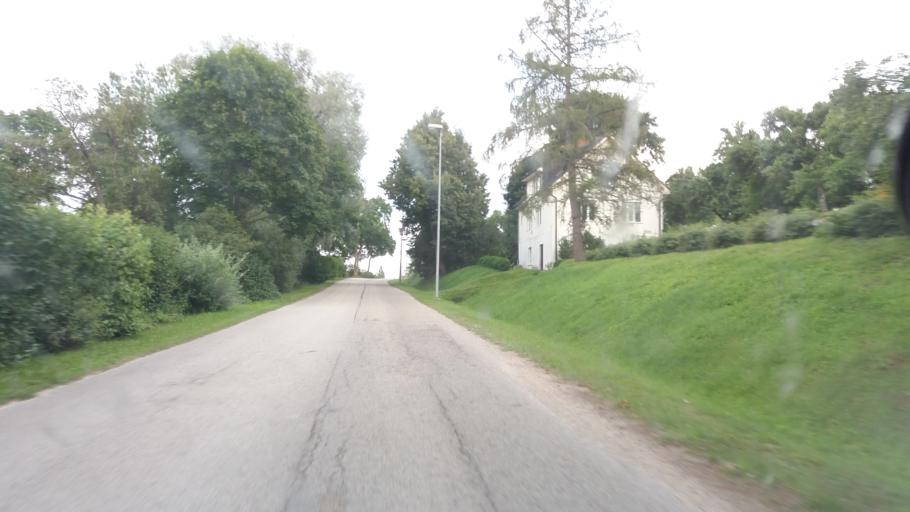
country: LV
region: Talsu Rajons
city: Sabile
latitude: 57.0386
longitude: 22.5706
